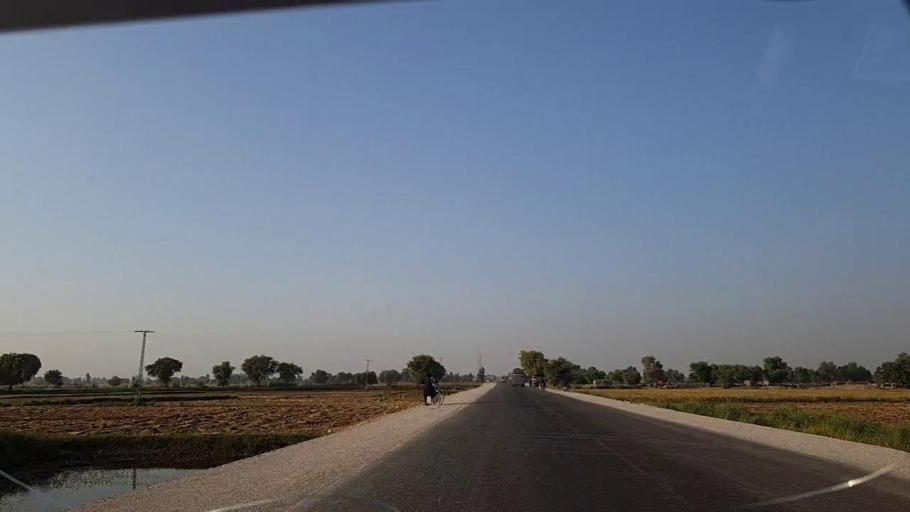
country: PK
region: Sindh
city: Rustam jo Goth
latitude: 27.9536
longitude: 68.8084
